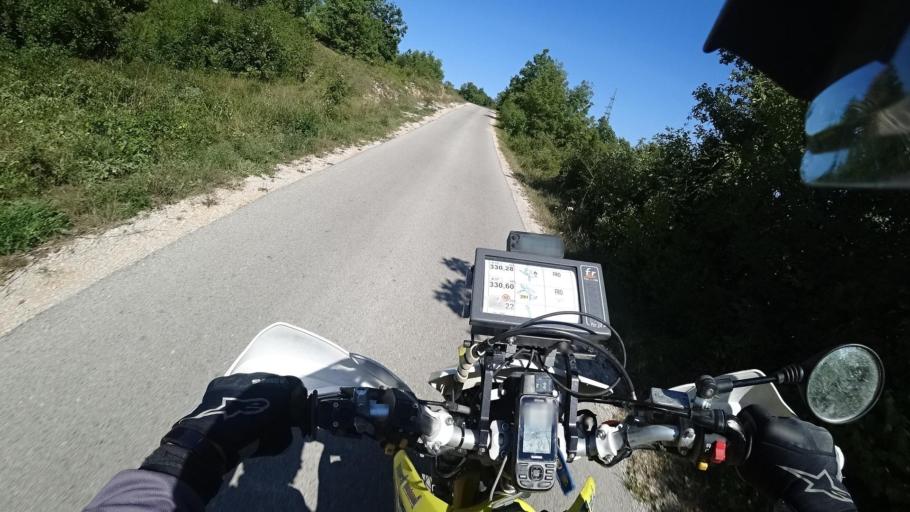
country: HR
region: Licko-Senjska
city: Otocac
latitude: 44.7357
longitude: 15.3625
